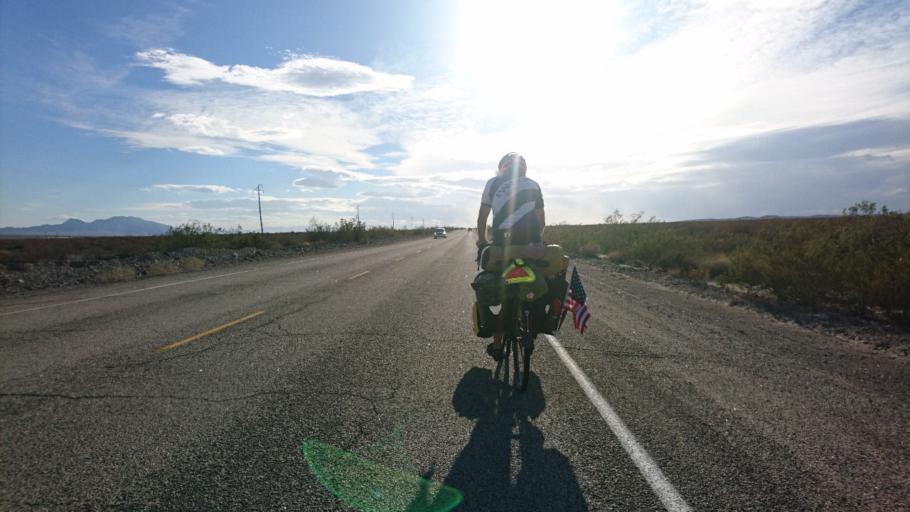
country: US
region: California
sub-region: San Bernardino County
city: Needles
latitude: 34.6812
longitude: -115.3250
